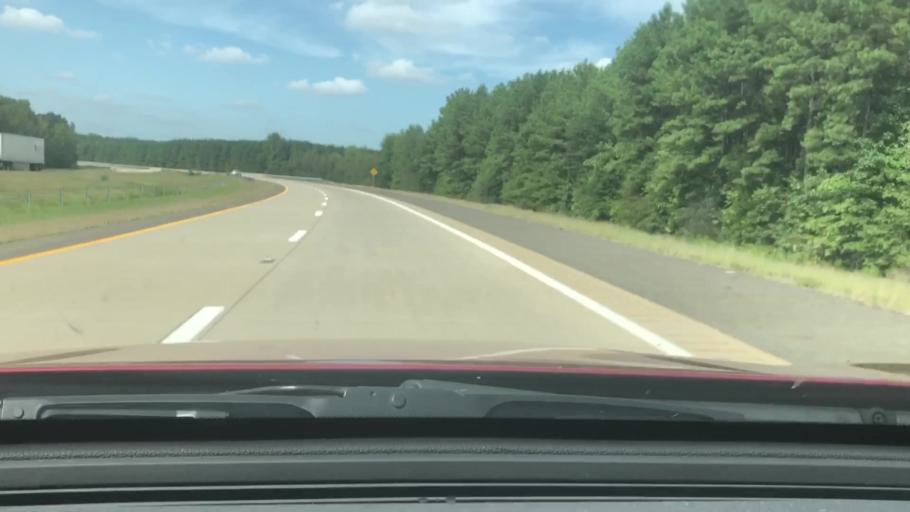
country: US
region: Texas
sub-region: Bowie County
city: Texarkana
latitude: 33.2380
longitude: -93.8727
